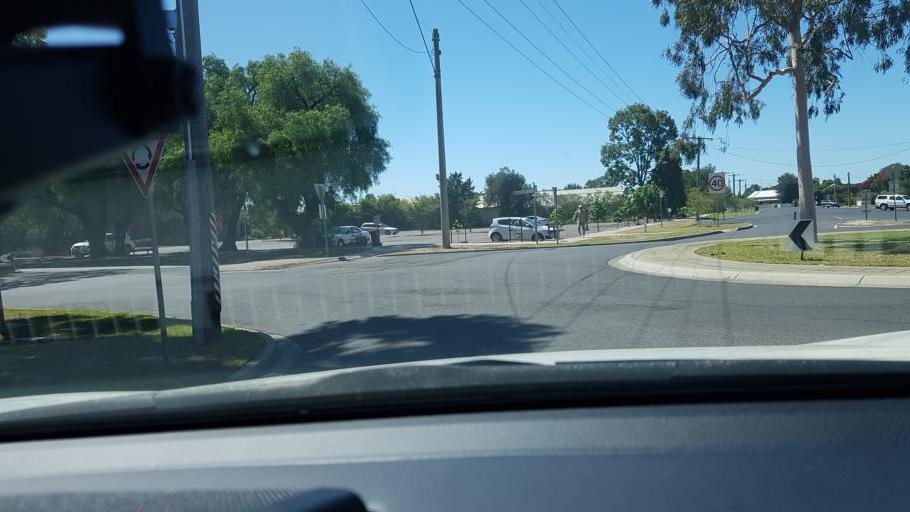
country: AU
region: Victoria
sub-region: Horsham
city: Horsham
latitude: -36.7143
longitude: 142.2020
